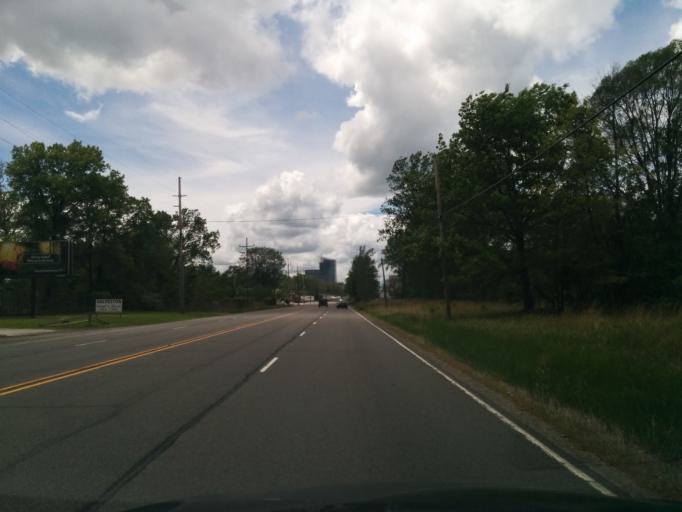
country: US
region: Indiana
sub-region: LaPorte County
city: Michigan City
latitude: 41.7242
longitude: -86.8798
